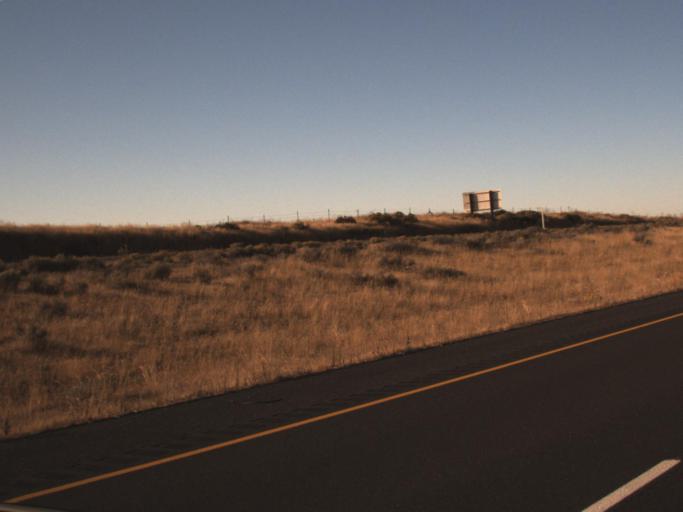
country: US
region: Washington
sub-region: Franklin County
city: Connell
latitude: 46.6386
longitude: -118.8658
